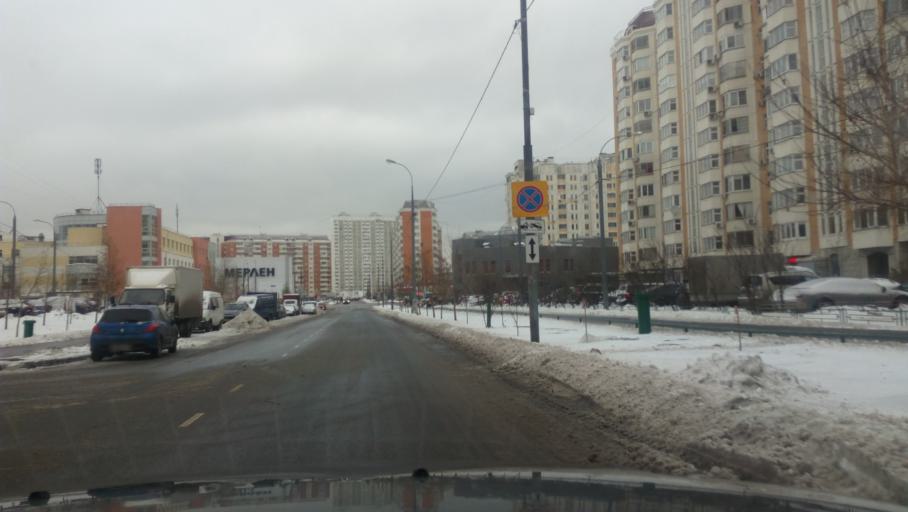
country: RU
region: Moscow
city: Nekrasovka
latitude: 55.7123
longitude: 37.8859
